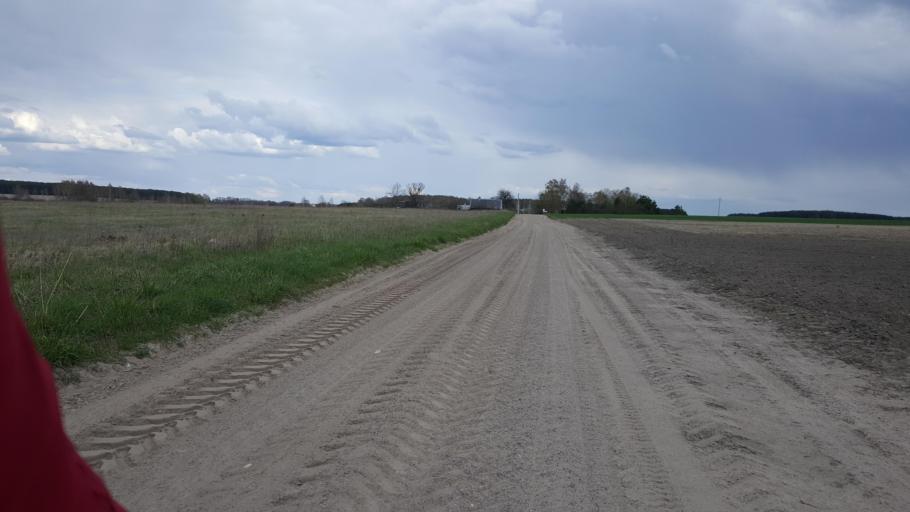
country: BY
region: Brest
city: Kamyanyets
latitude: 52.4032
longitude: 23.7240
